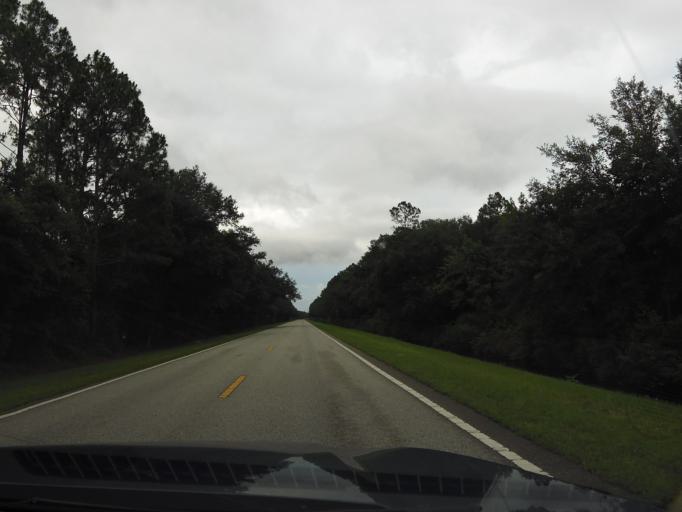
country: US
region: Florida
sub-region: Saint Johns County
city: Saint Augustine South
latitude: 29.8544
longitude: -81.4670
